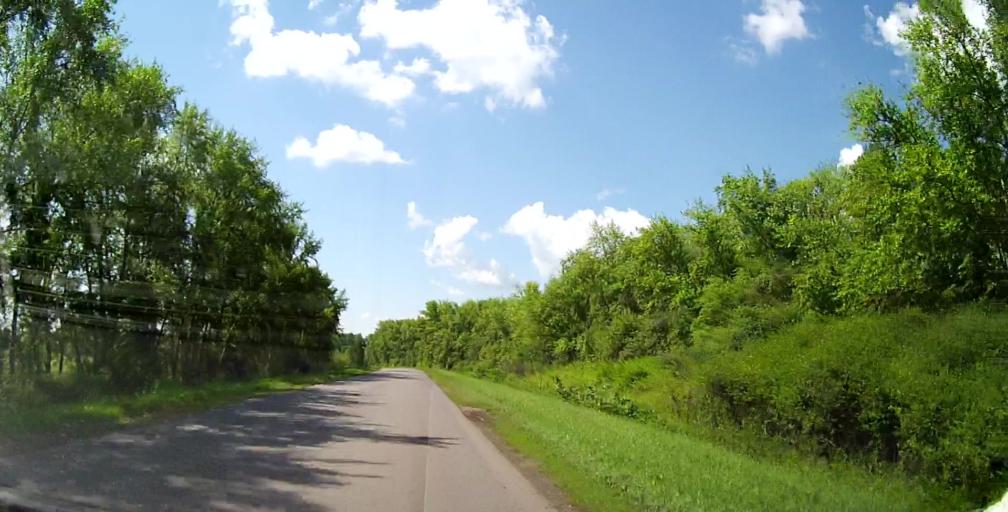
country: RU
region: Lipetsk
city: Chaplygin
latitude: 53.3082
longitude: 39.9541
